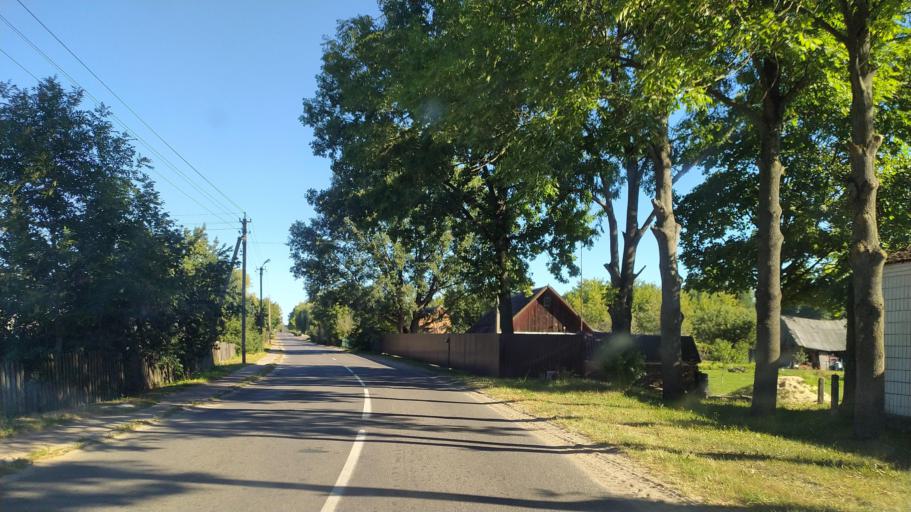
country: BY
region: Brest
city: Pruzhany
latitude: 52.4851
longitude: 24.7074
